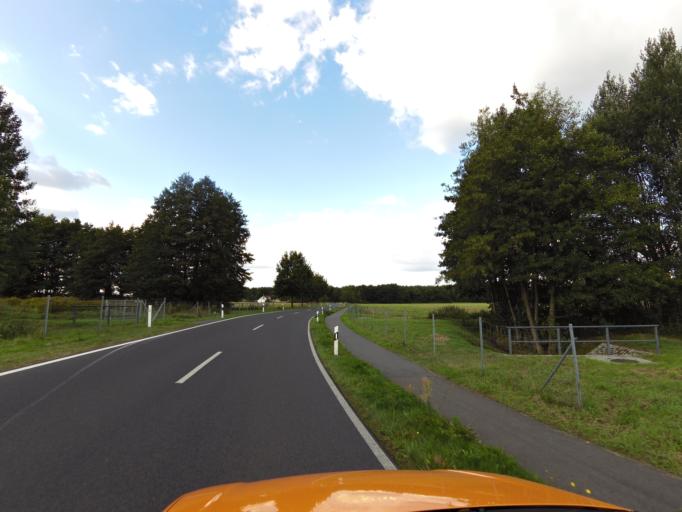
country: DE
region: Brandenburg
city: Luckenwalde
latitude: 52.1075
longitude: 13.1729
